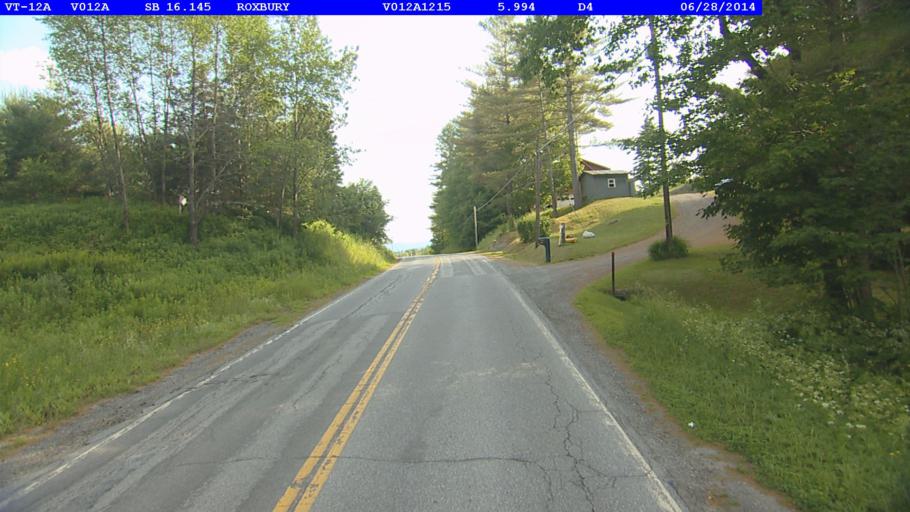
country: US
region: Vermont
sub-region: Washington County
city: Northfield
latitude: 44.1110
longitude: -72.7266
